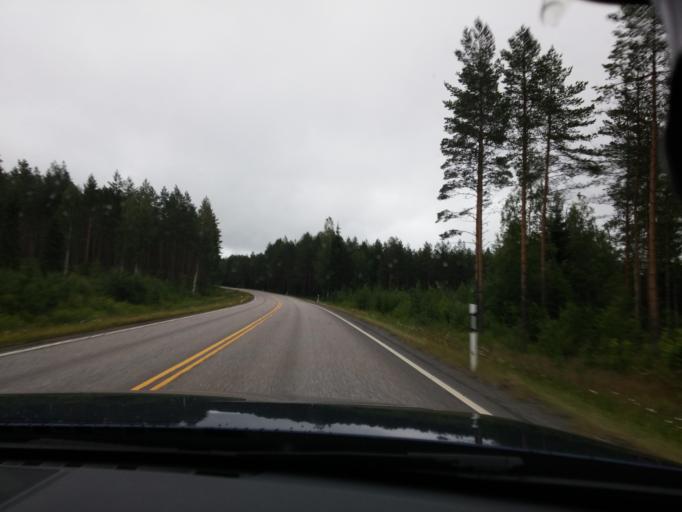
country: FI
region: Pirkanmaa
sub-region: Ylae-Pirkanmaa
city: Vilppula
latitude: 61.9223
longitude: 24.5394
